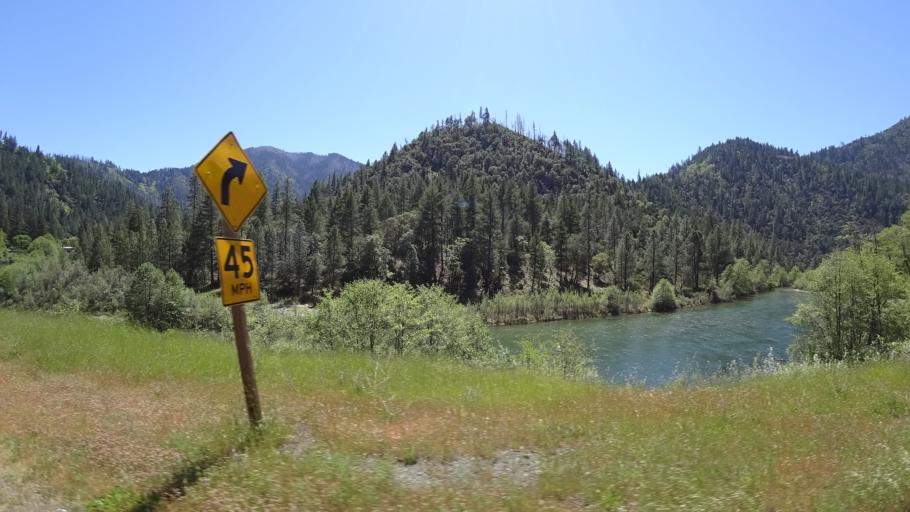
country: US
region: California
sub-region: Trinity County
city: Hayfork
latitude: 40.7848
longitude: -123.3383
